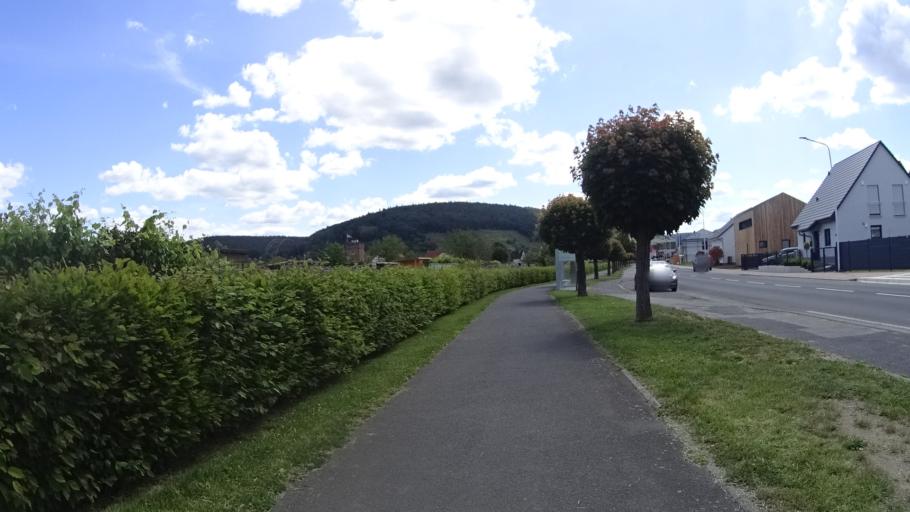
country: DE
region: Bavaria
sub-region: Regierungsbezirk Unterfranken
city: Worth am Main
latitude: 49.7992
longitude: 9.1528
